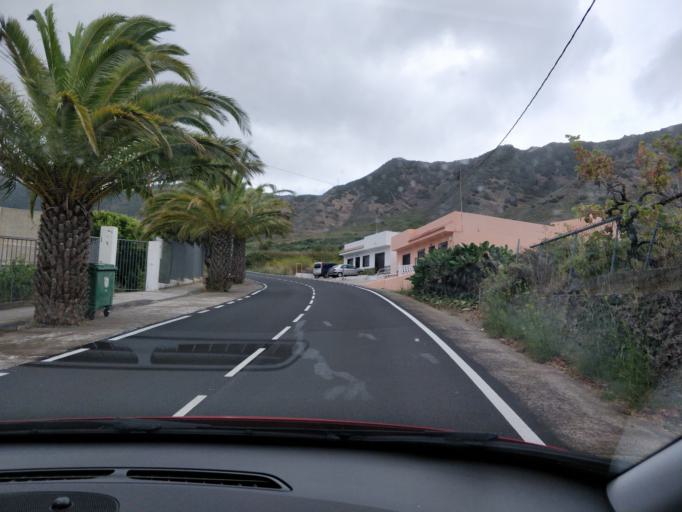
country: ES
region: Canary Islands
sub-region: Provincia de Santa Cruz de Tenerife
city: Tanque
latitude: 28.3395
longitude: -16.8513
